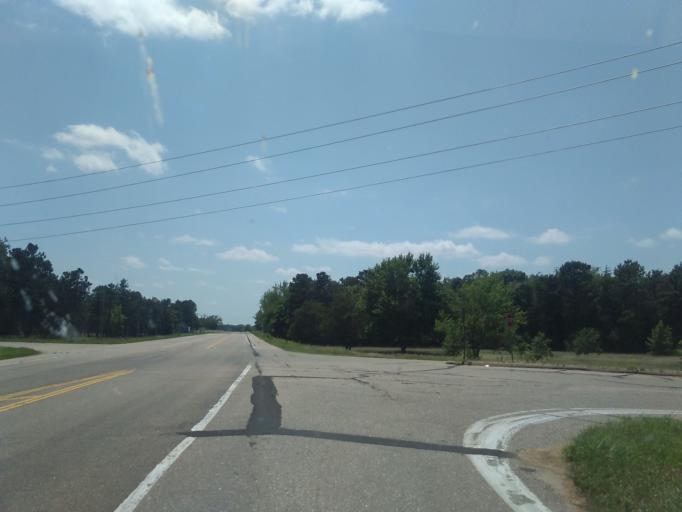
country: US
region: Nebraska
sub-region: Gosper County
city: Elwood
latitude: 40.6821
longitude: -99.8275
